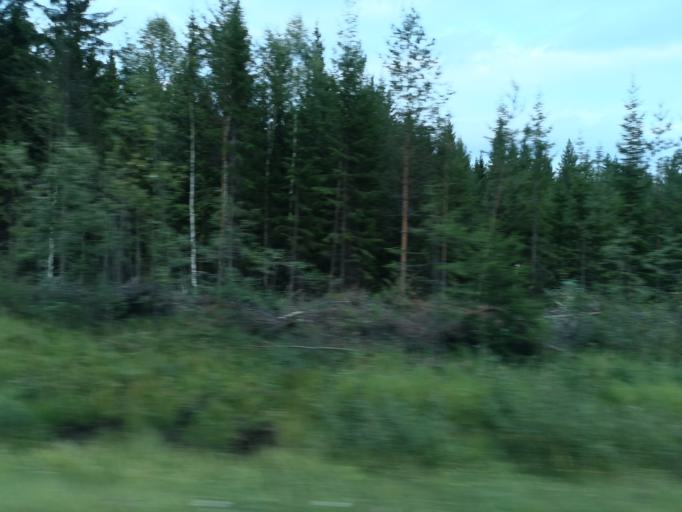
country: FI
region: Central Finland
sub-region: Joutsa
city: Leivonmaeki
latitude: 61.9038
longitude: 26.1162
